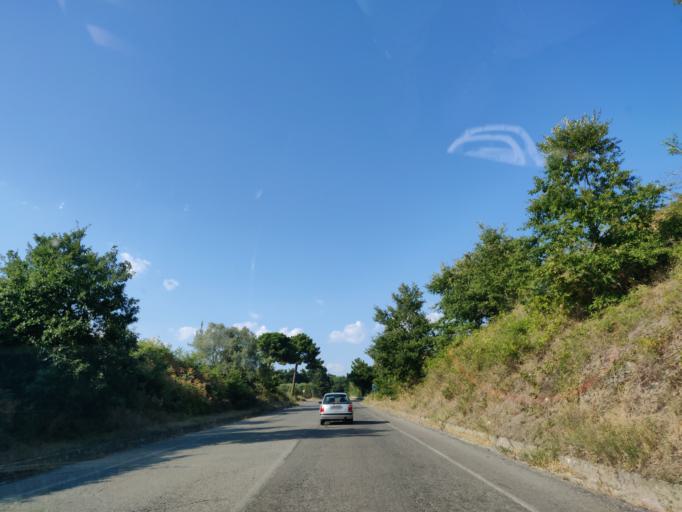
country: IT
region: Latium
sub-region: Provincia di Viterbo
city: Valentano
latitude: 42.5893
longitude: 11.8362
